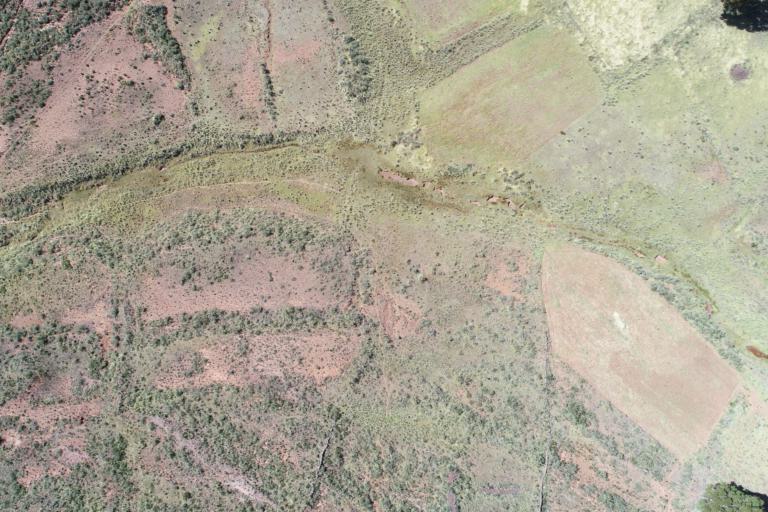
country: BO
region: La Paz
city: Tiahuanaco
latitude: -16.6062
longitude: -68.7735
